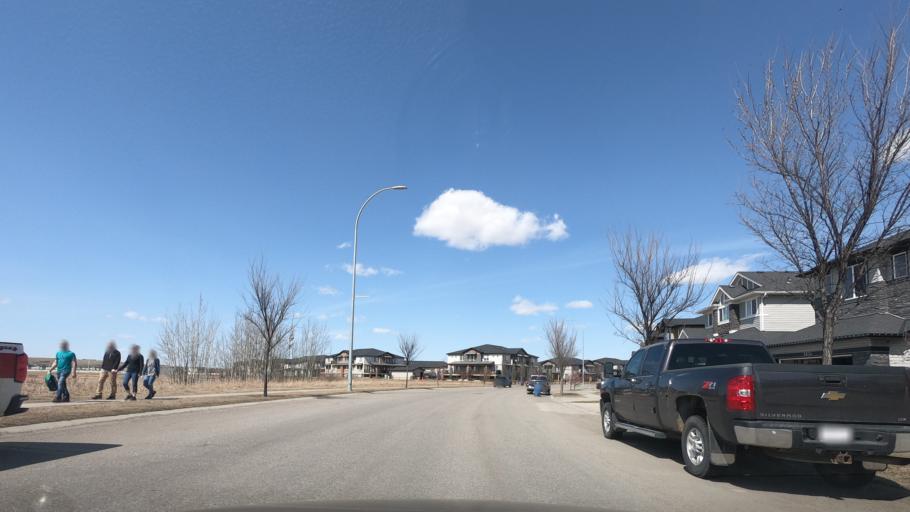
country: CA
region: Alberta
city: Airdrie
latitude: 51.2658
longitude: -114.0319
